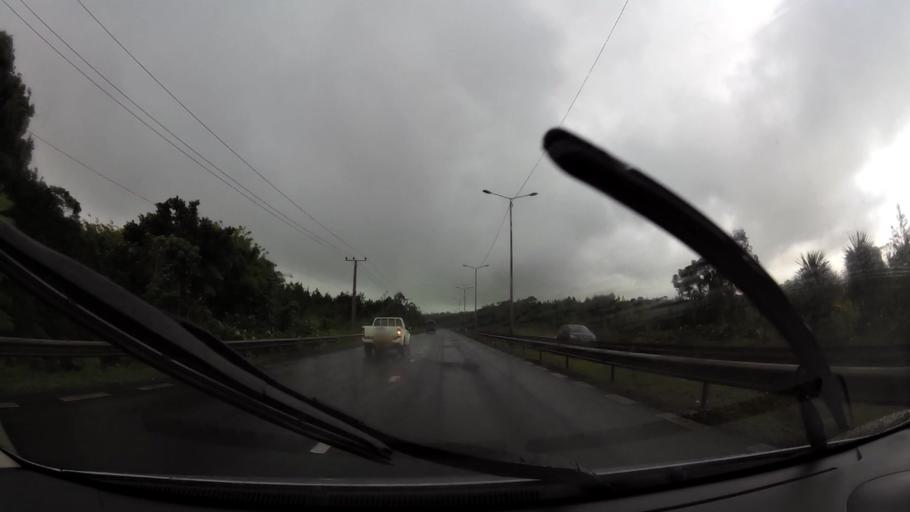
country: MU
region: Plaines Wilhems
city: Midlands
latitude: -20.3263
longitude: 57.5457
